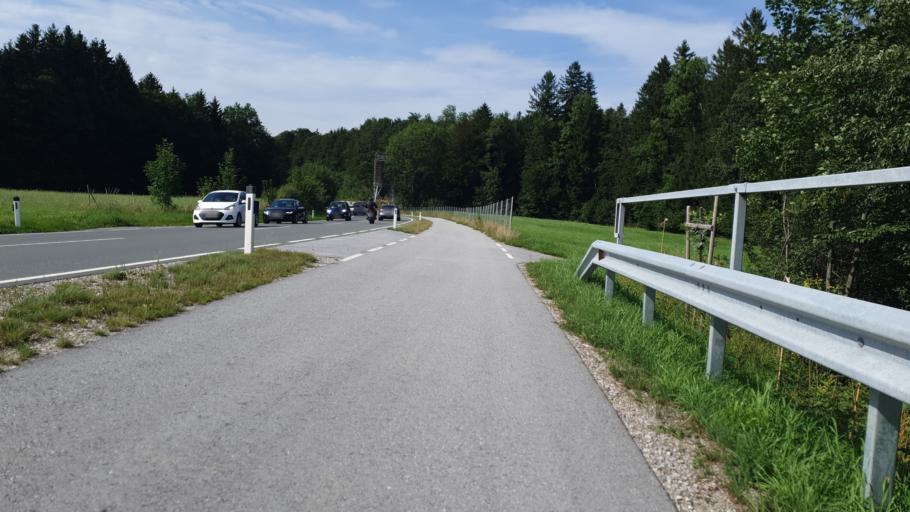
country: AT
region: Salzburg
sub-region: Politischer Bezirk Salzburg-Umgebung
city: Eugendorf
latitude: 47.8734
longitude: 13.1267
